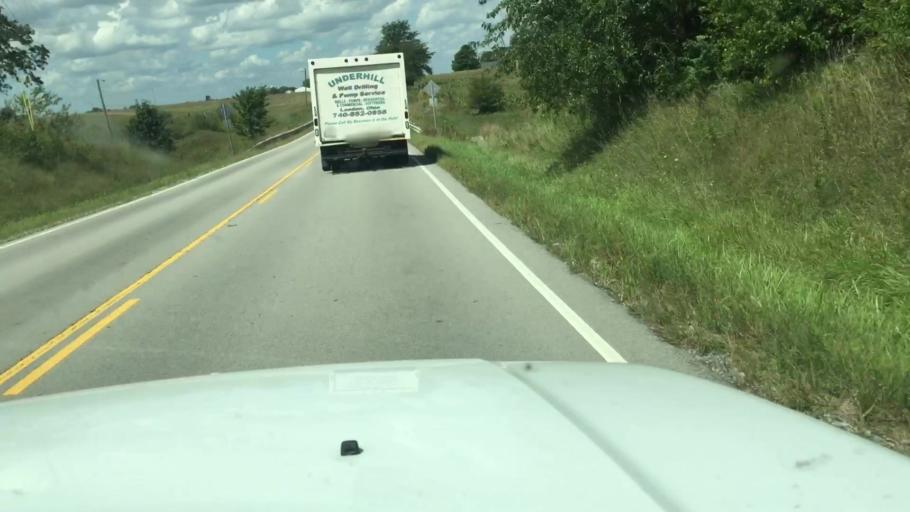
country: US
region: Ohio
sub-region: Madison County
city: Bethel
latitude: 39.8160
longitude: -83.3542
